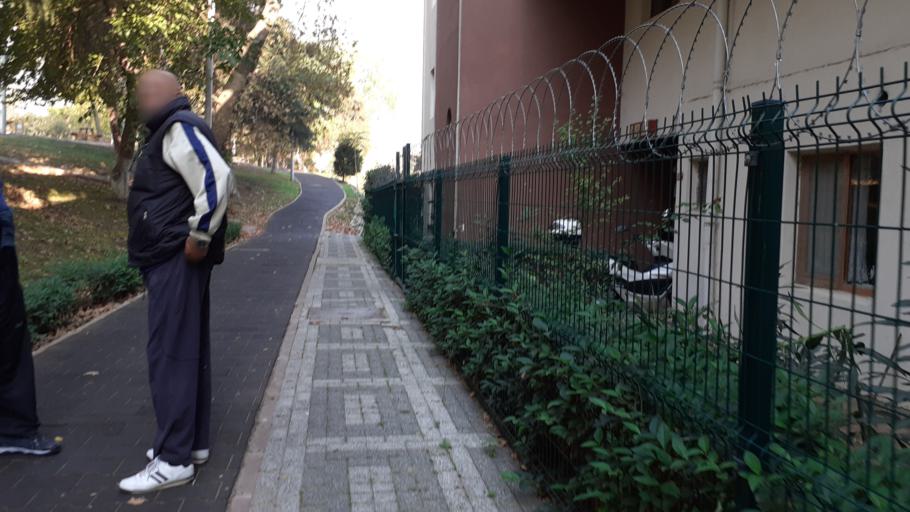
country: TR
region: Istanbul
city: Mahmutbey
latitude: 41.0486
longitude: 28.7960
